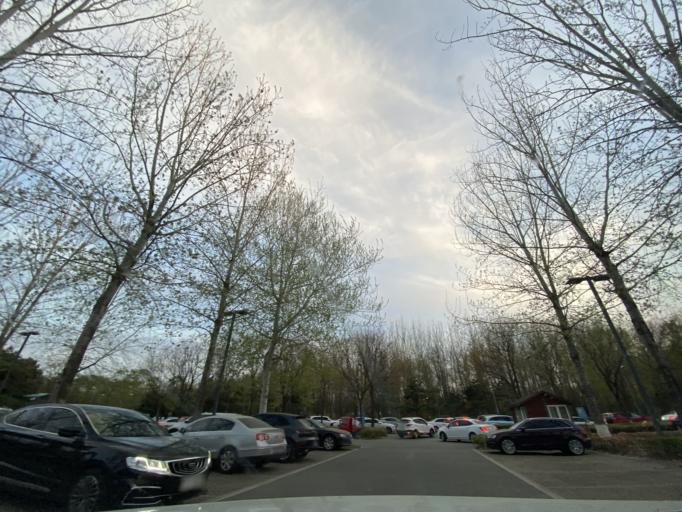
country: CN
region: Beijing
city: Qinghe
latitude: 40.0127
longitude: 116.3699
